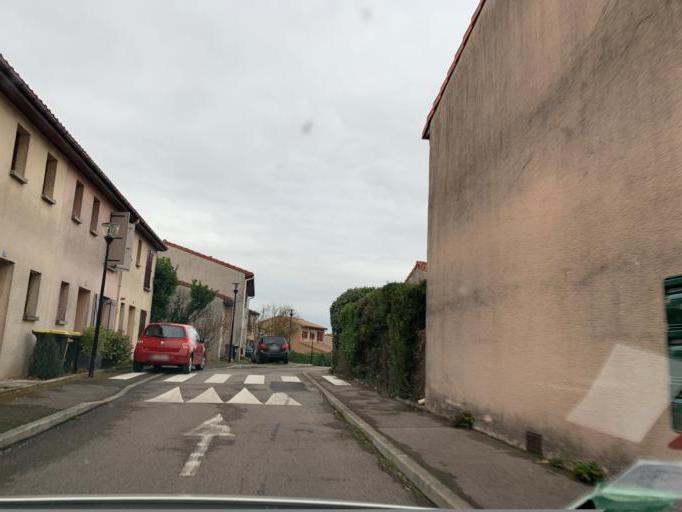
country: FR
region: Rhone-Alpes
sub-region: Departement du Rhone
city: Rillieux-la-Pape
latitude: 45.8350
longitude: 4.9084
